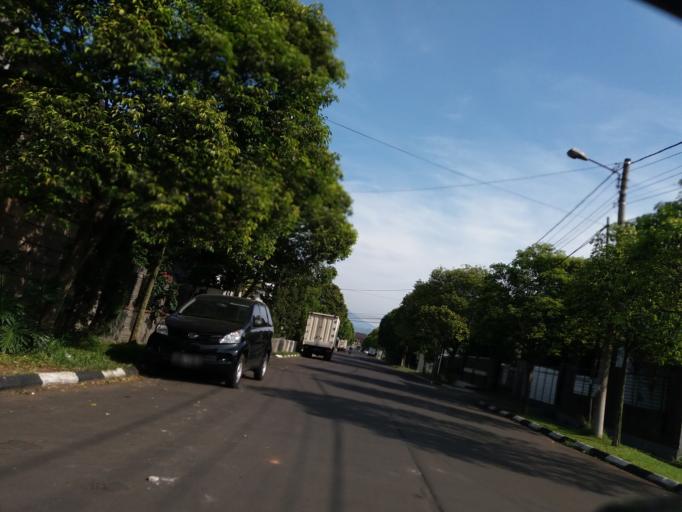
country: ID
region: West Java
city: Bandung
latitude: -6.9571
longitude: 107.6339
